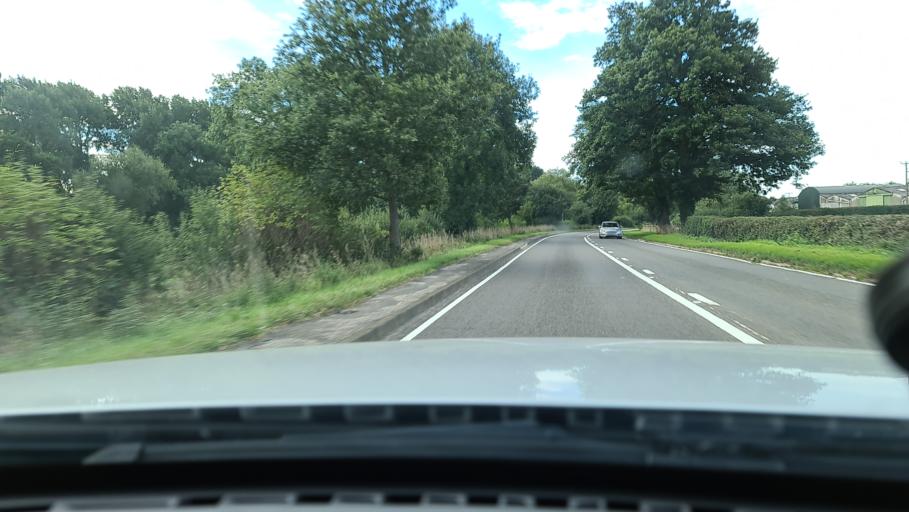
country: GB
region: England
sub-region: Warwickshire
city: Shipston on Stour
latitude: 52.0864
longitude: -1.6245
